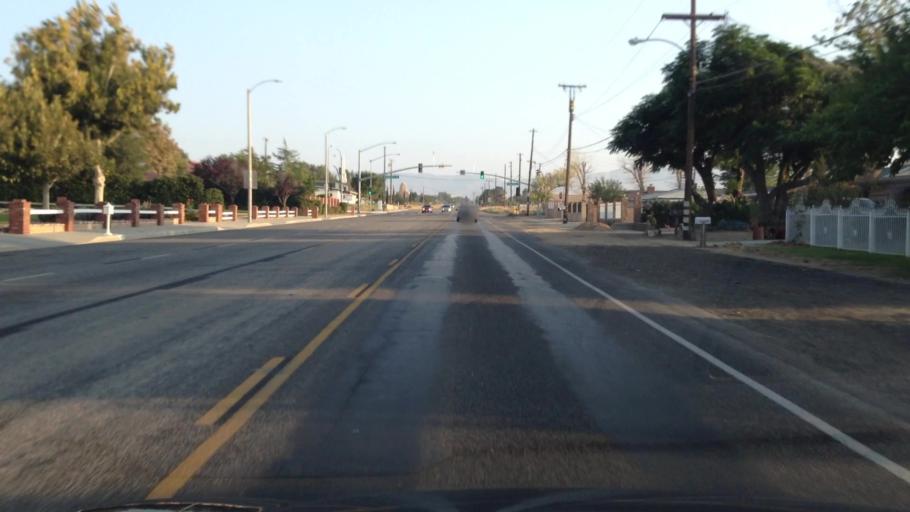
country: US
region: California
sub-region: Los Angeles County
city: Quartz Hill
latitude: 34.6544
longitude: -118.1833
